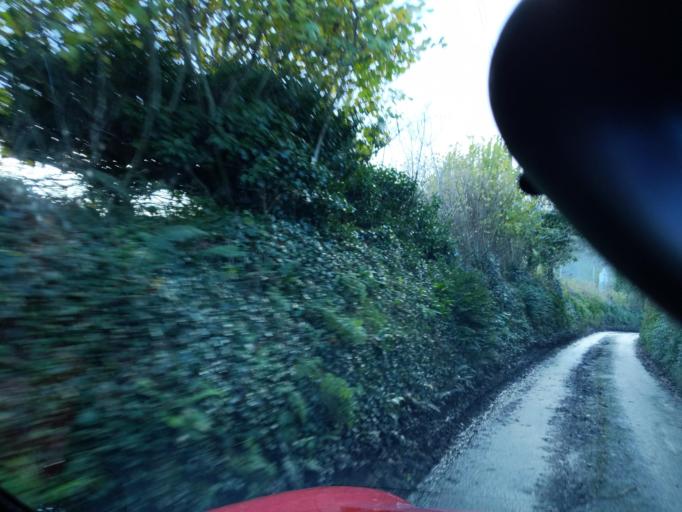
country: GB
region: England
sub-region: Cornwall
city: Looe
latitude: 50.3440
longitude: -4.4782
